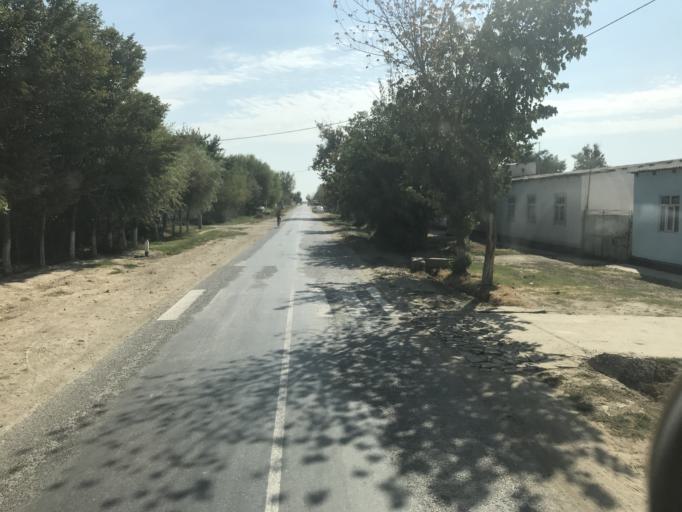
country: KZ
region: Ongtustik Qazaqstan
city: Myrzakent
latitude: 40.6643
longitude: 68.6216
